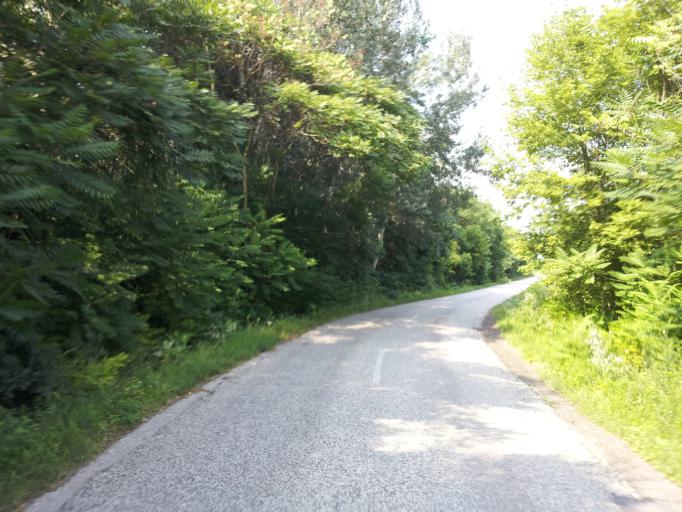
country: HU
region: Pest
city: Szigetujfalu
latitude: 47.2060
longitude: 18.9125
